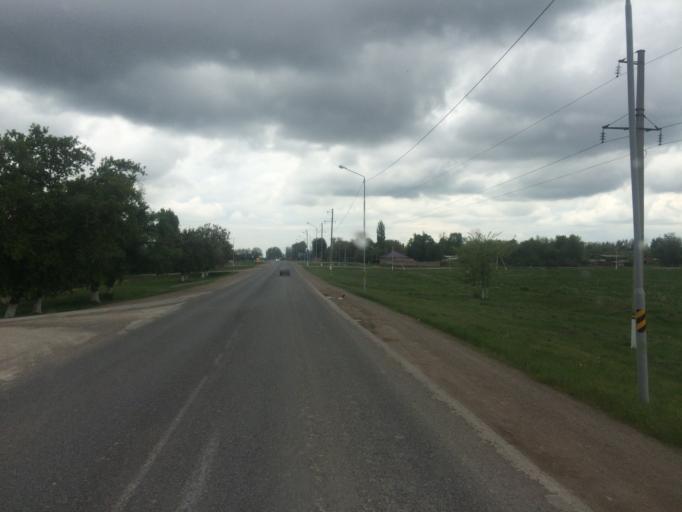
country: KZ
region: Zhambyl
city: Georgiyevka
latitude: 43.1447
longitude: 74.6140
